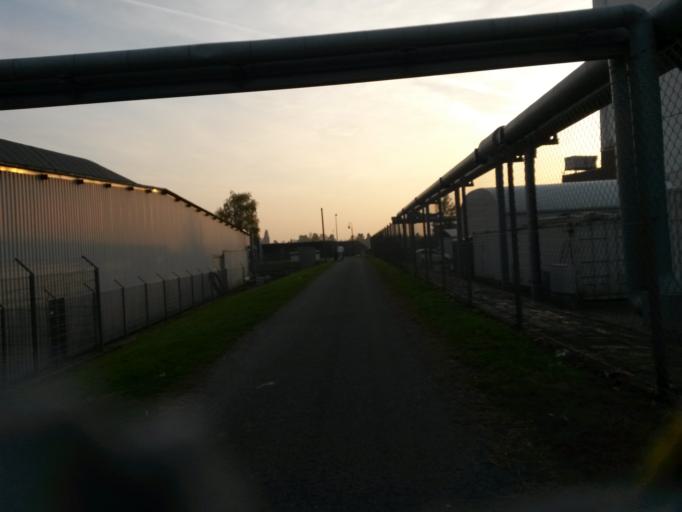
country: DE
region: Bremen
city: Bremen
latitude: 53.0598
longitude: 8.8754
